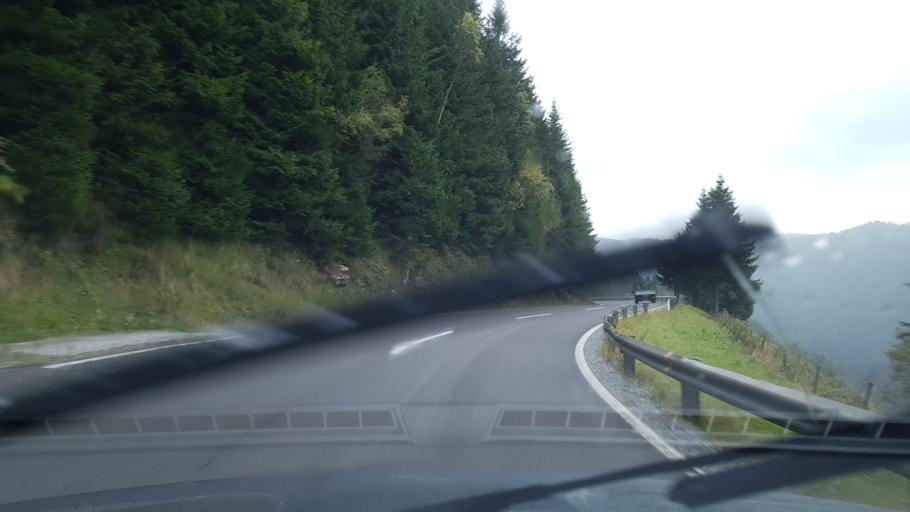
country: AT
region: Styria
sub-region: Politischer Bezirk Voitsberg
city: Salla
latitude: 47.1164
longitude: 14.9260
